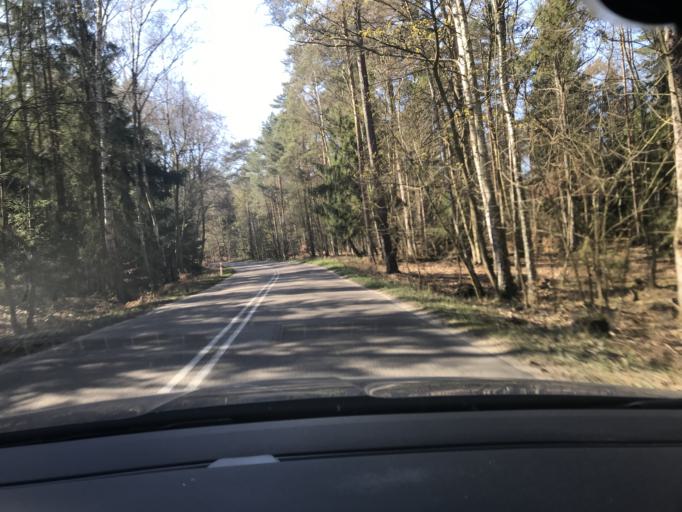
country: PL
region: Pomeranian Voivodeship
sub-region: Powiat nowodworski
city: Krynica Morska
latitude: 54.3677
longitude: 19.3928
